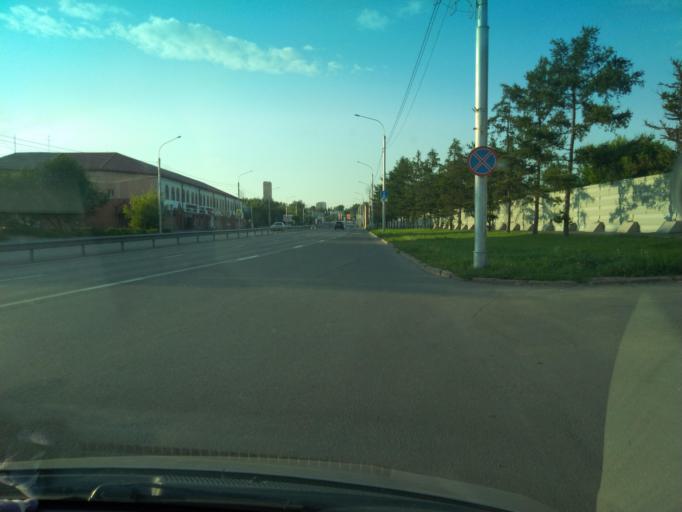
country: RU
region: Krasnoyarskiy
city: Krasnoyarsk
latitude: 56.0206
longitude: 92.8853
